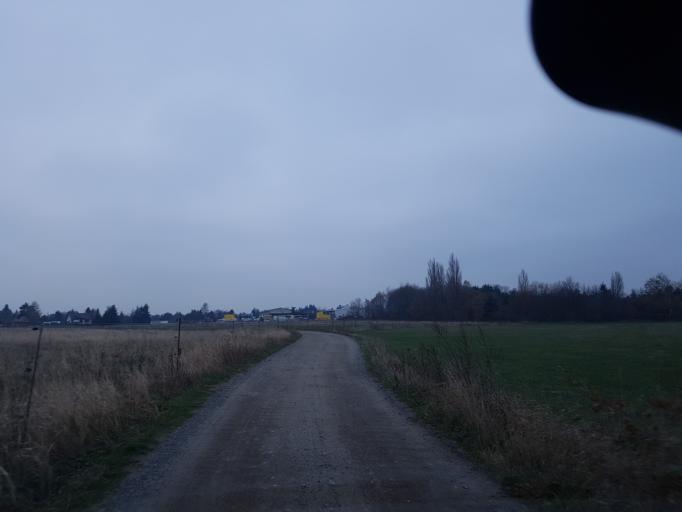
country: DE
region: Brandenburg
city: Finsterwalde
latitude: 51.6181
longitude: 13.7308
